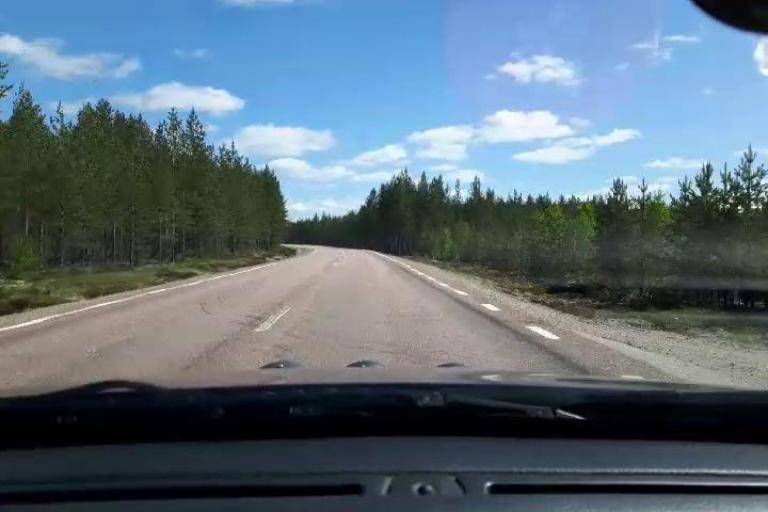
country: SE
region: Gaevleborg
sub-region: Ljusdals Kommun
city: Farila
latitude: 61.9388
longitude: 15.4877
